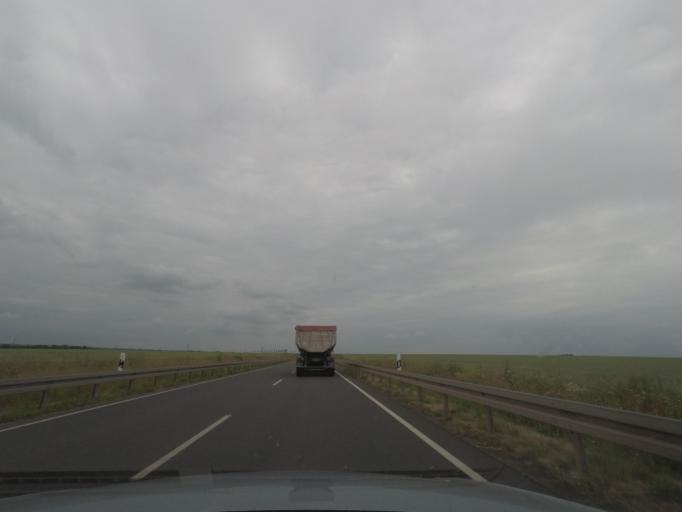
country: DE
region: Saxony-Anhalt
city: Suplingen
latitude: 52.2434
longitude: 11.3214
